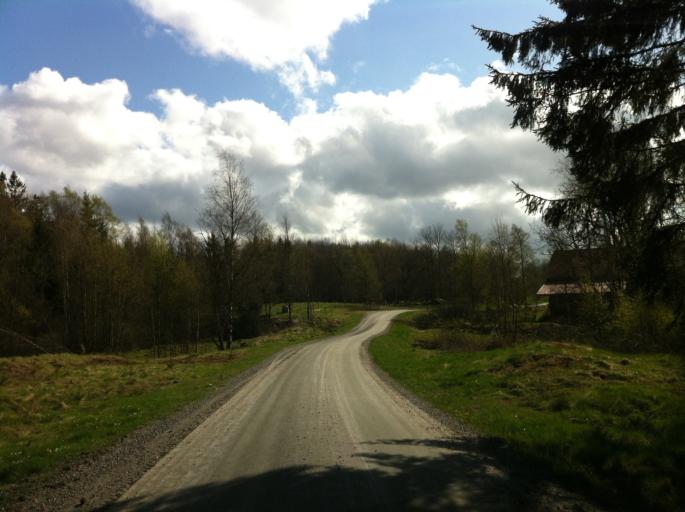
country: SE
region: Vaestra Goetaland
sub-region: Bollebygds Kommun
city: Bollebygd
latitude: 57.7715
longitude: 12.5925
